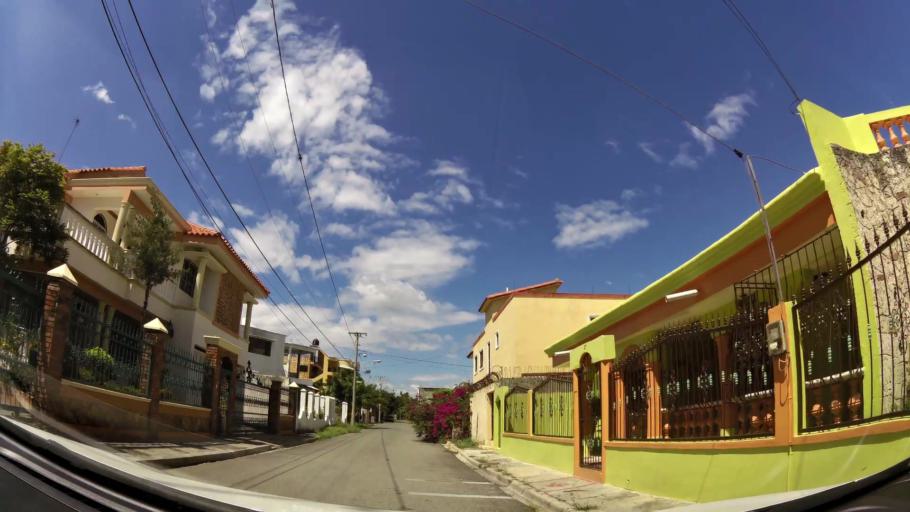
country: DO
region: San Cristobal
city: San Cristobal
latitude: 18.4127
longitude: -70.0904
